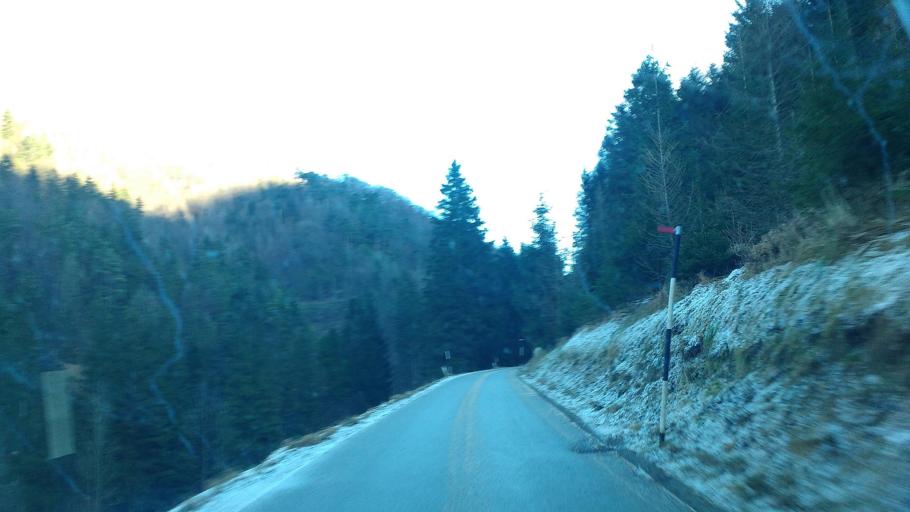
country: AT
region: Upper Austria
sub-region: Politischer Bezirk Kirchdorf an der Krems
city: Micheldorf in Oberoesterreich
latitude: 47.9009
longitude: 14.2026
